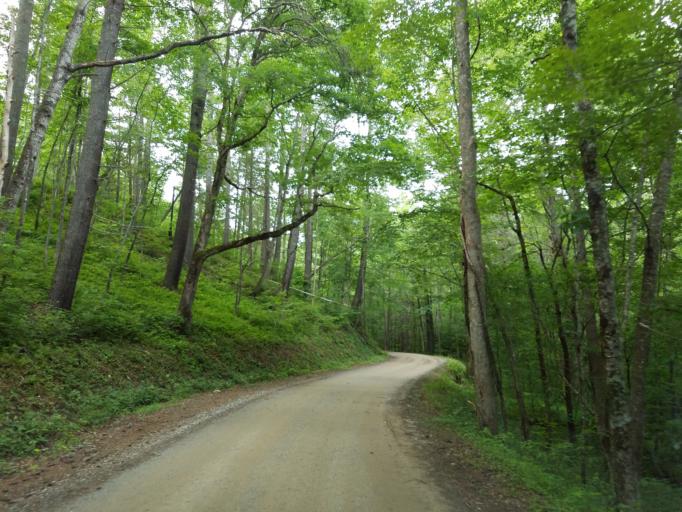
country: US
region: Georgia
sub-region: Union County
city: Blairsville
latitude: 34.7715
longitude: -84.0676
